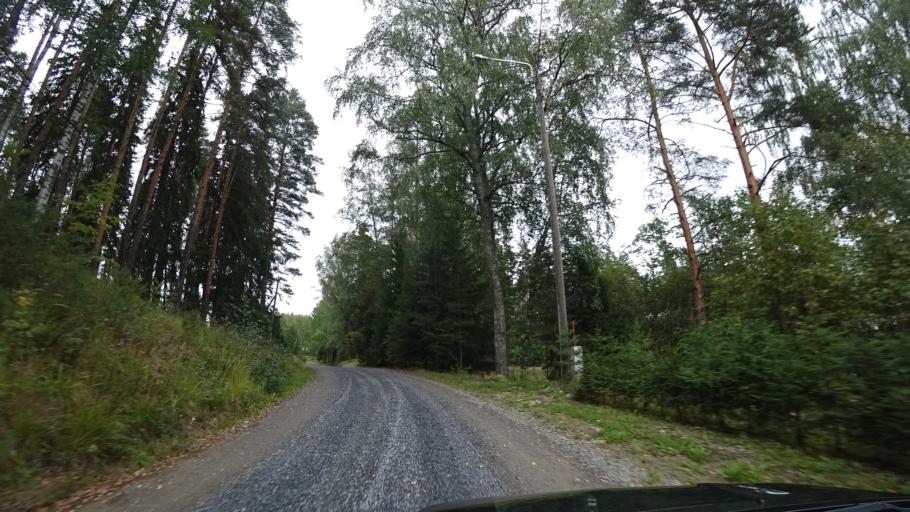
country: FI
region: Haeme
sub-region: Haemeenlinna
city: Lammi
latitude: 61.1226
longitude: 24.9836
